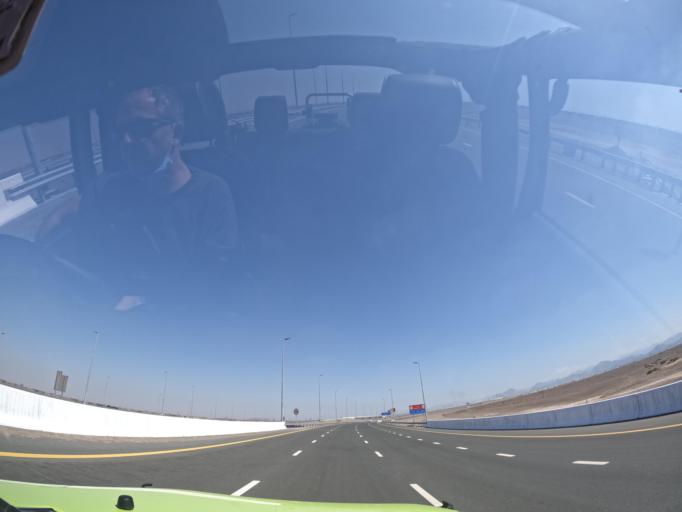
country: AE
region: Ash Shariqah
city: Adh Dhayd
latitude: 25.1130
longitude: 55.9360
